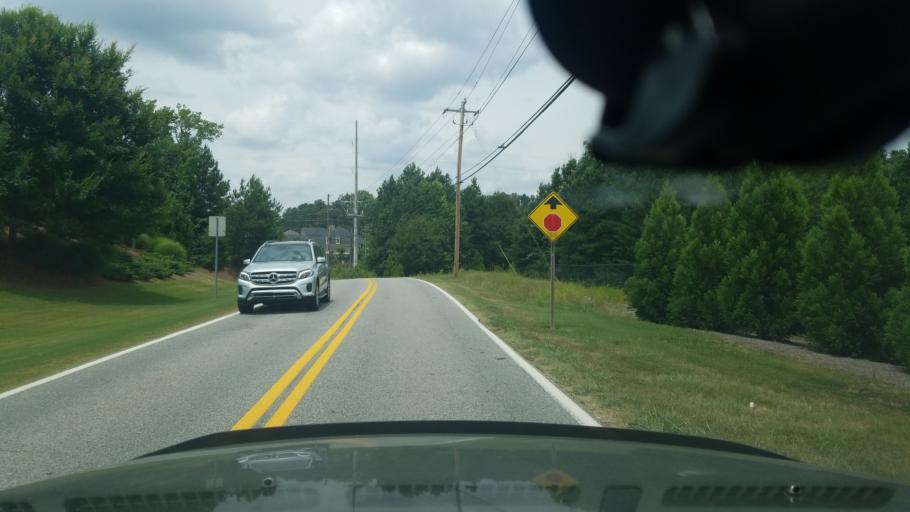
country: US
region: Georgia
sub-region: Fulton County
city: Milton
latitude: 34.1545
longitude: -84.2209
